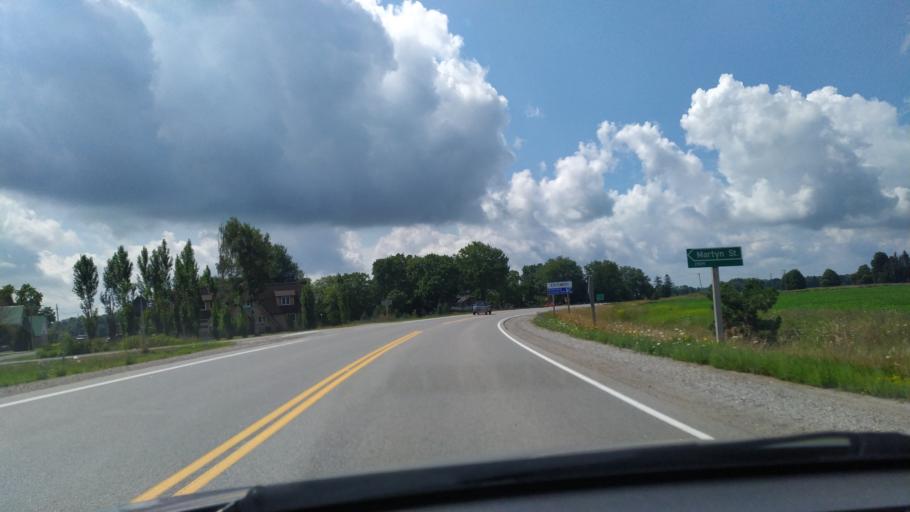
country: CA
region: Ontario
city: Huron East
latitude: 43.3881
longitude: -81.2595
